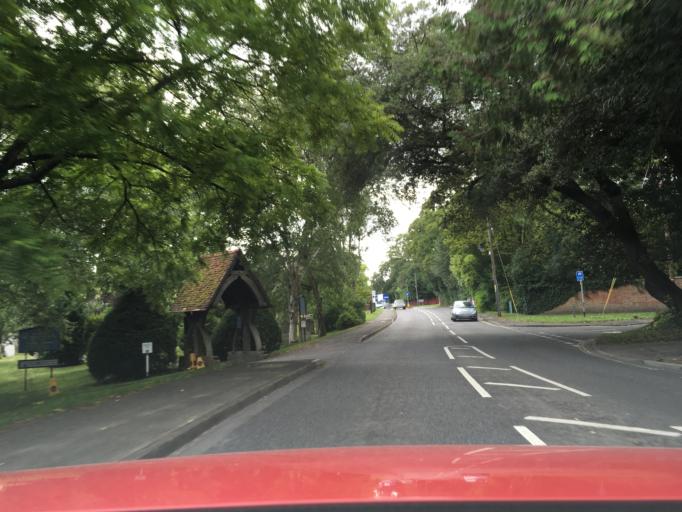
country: GB
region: England
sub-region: Hampshire
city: Kings Worthy
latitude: 51.0887
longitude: -1.2975
